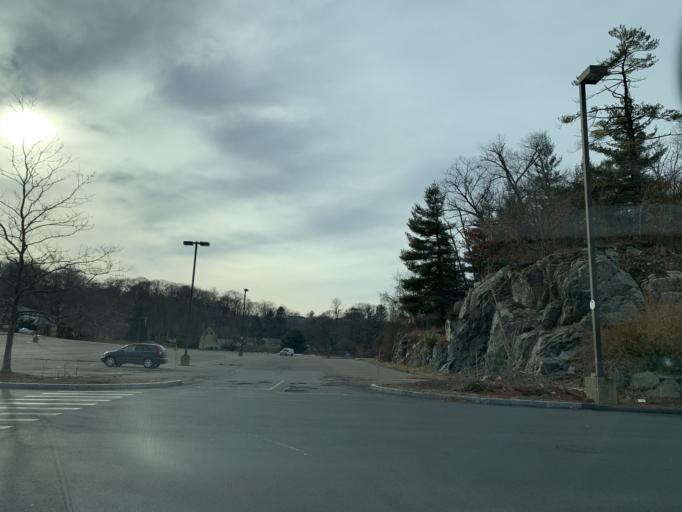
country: US
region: Massachusetts
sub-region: Essex County
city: Saugus
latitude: 42.4596
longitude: -71.0281
